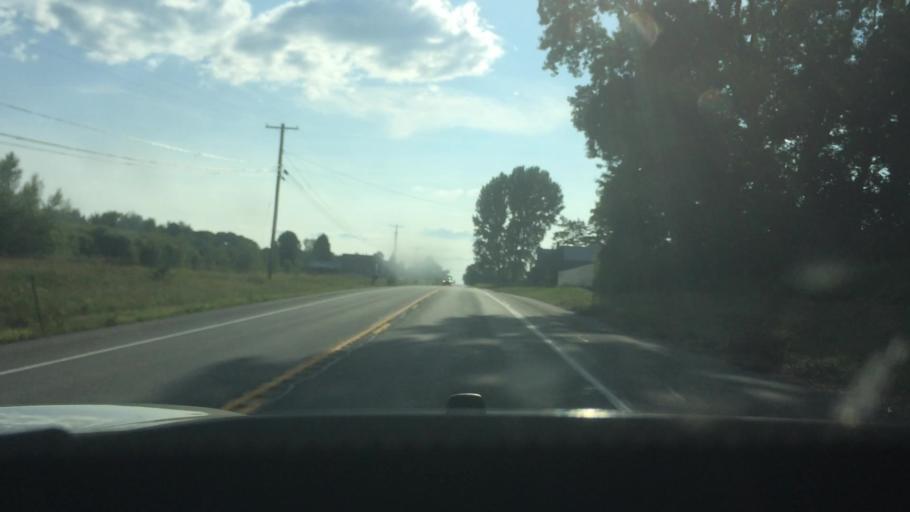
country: US
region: New York
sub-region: St. Lawrence County
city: Potsdam
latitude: 44.6850
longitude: -74.8053
